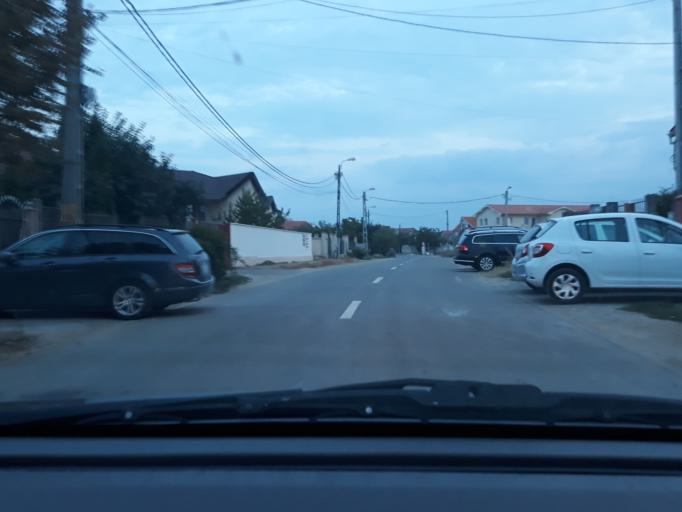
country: RO
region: Bihor
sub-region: Comuna Biharea
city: Oradea
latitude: 47.0275
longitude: 21.9357
